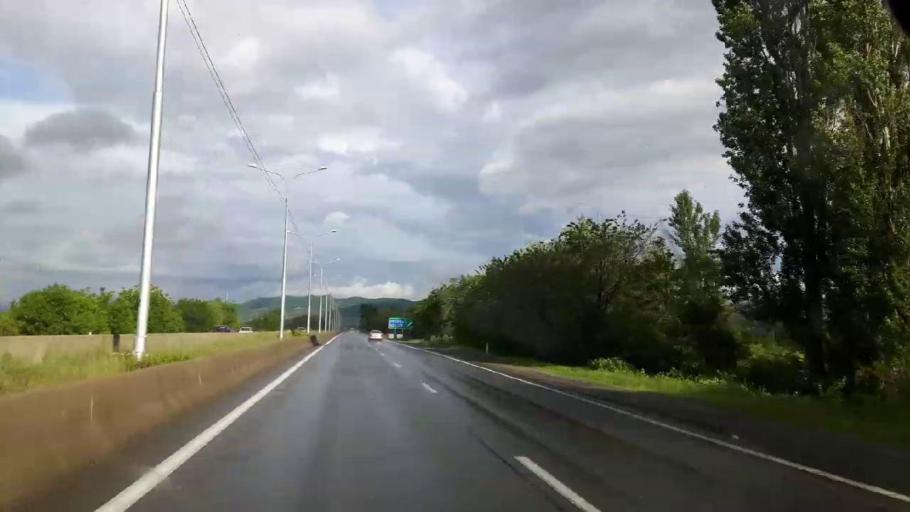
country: GE
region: Shida Kartli
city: Kaspi
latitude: 41.9207
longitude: 44.5479
